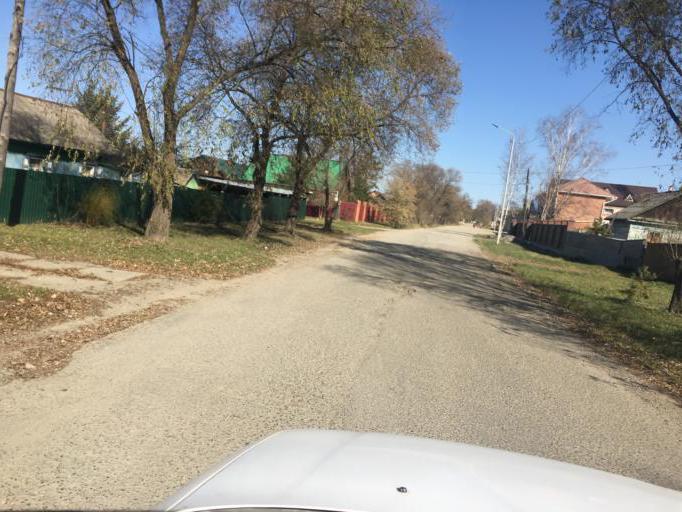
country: RU
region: Primorskiy
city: Dal'nerechensk
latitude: 45.9244
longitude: 133.7433
